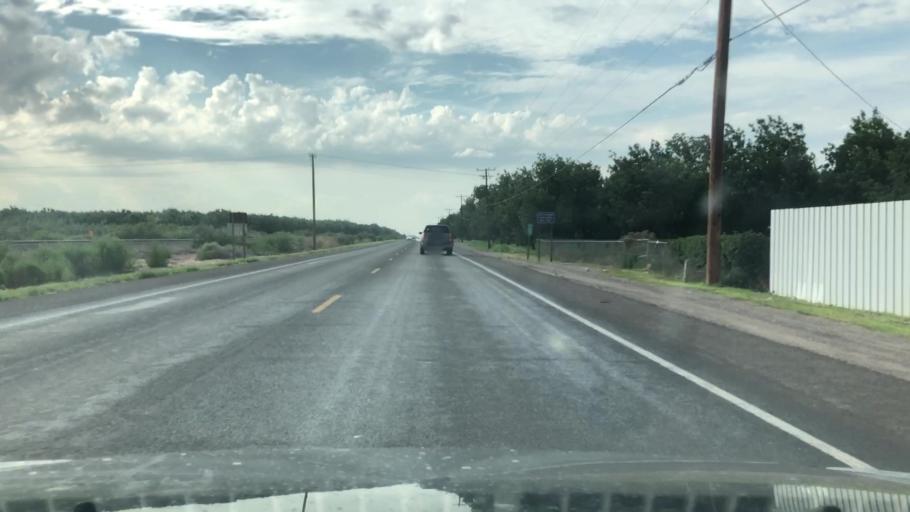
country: US
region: New Mexico
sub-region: Dona Ana County
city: Mesquite
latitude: 32.2101
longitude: -106.7253
